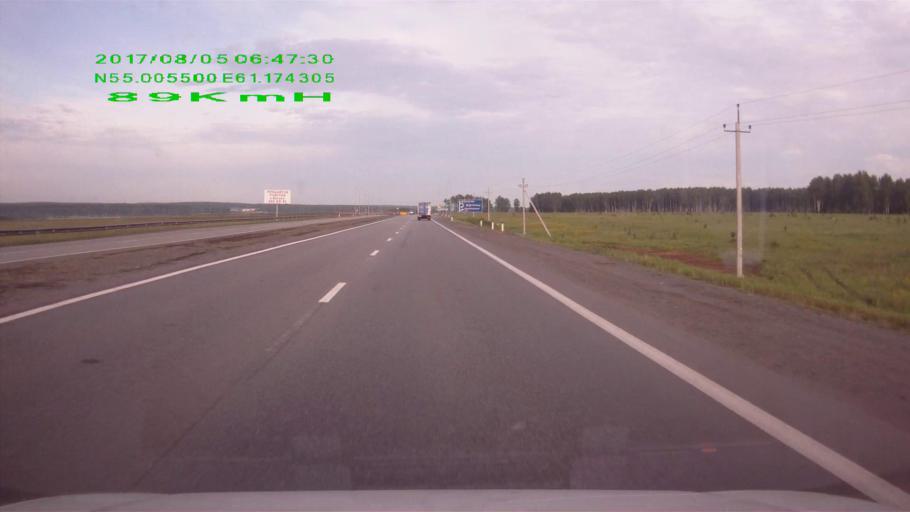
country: RU
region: Chelyabinsk
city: Poletayevo
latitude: 55.0055
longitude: 61.1741
